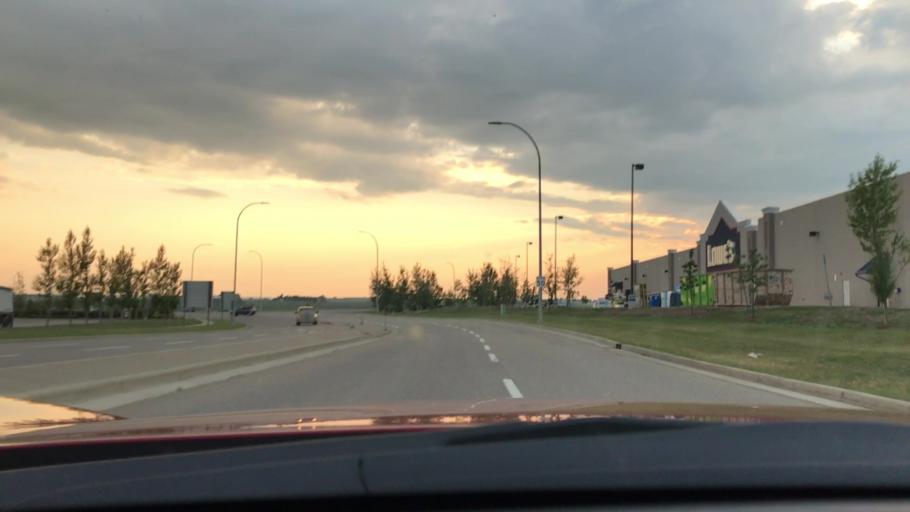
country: CA
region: Alberta
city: Airdrie
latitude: 51.2077
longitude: -113.9913
